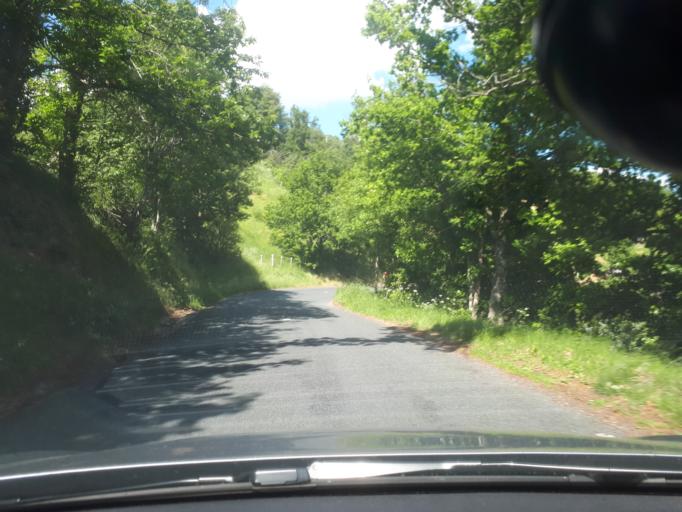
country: FR
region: Rhone-Alpes
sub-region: Departement du Rhone
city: Saint-Didier-sous-Riverie
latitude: 45.6355
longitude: 4.6228
